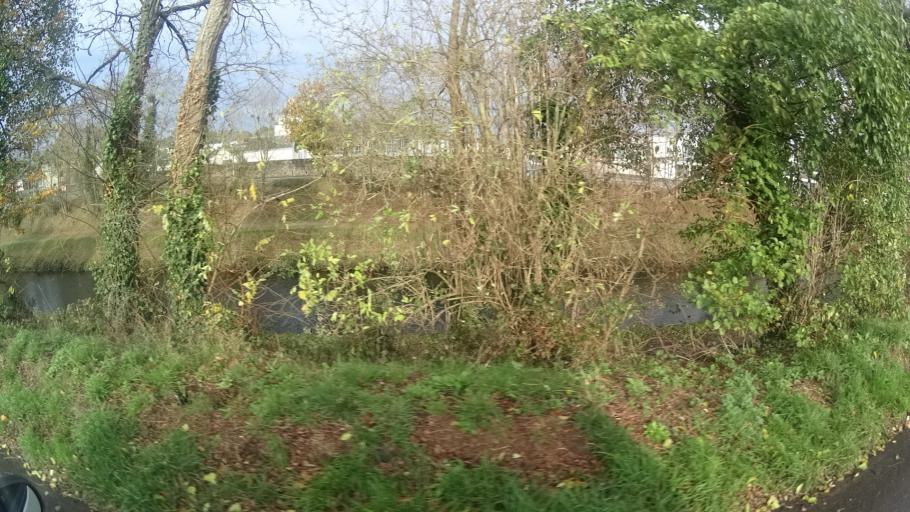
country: FR
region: Brittany
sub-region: Departement d'Ille-et-Vilaine
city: Redon
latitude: 47.6495
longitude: -2.0898
